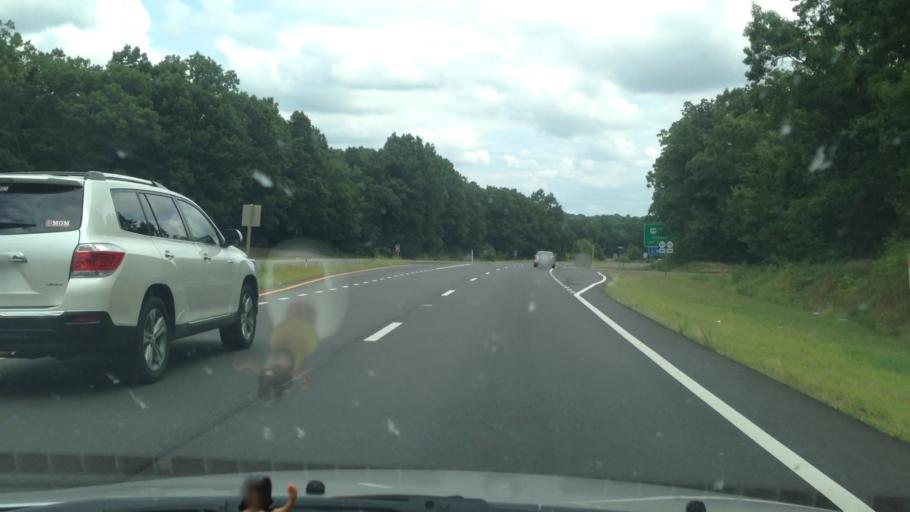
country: US
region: Virginia
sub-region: Pittsylvania County
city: Gretna
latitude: 36.9193
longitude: -79.3835
